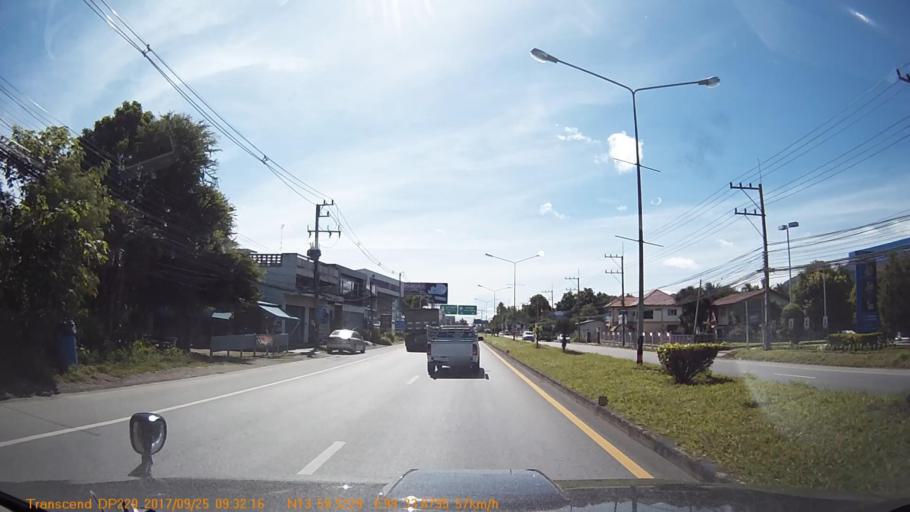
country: TH
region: Kanchanaburi
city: Kanchanaburi
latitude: 13.9919
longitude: 99.5648
